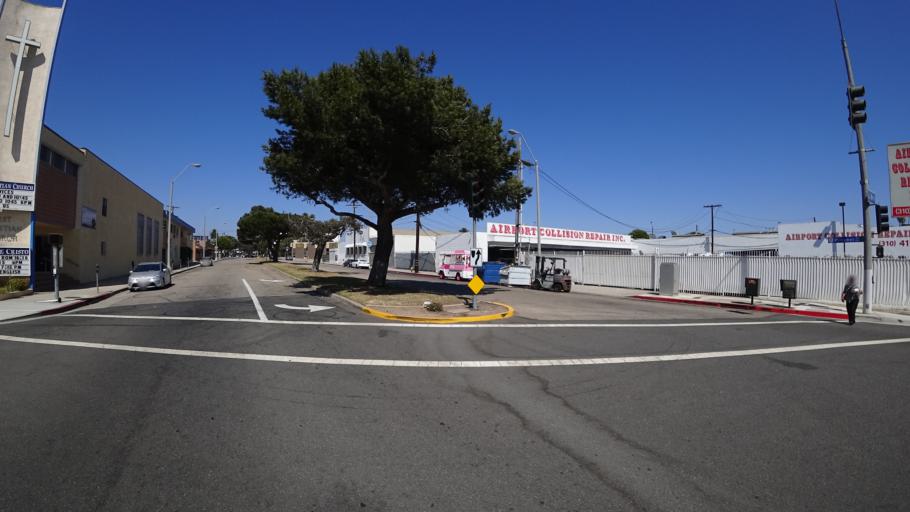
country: US
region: California
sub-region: Los Angeles County
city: Inglewood
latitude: 33.9581
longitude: -118.3532
